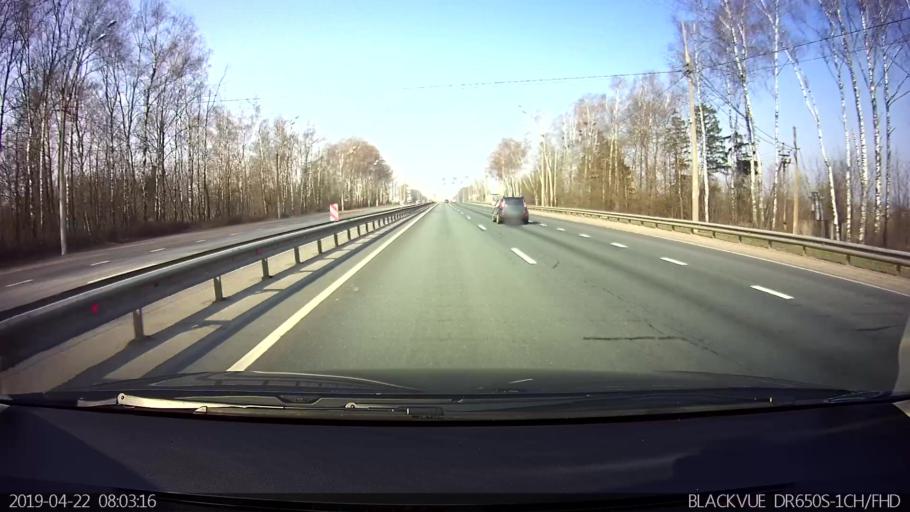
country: RU
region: Smolensk
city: Safonovo
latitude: 55.1179
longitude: 33.0471
